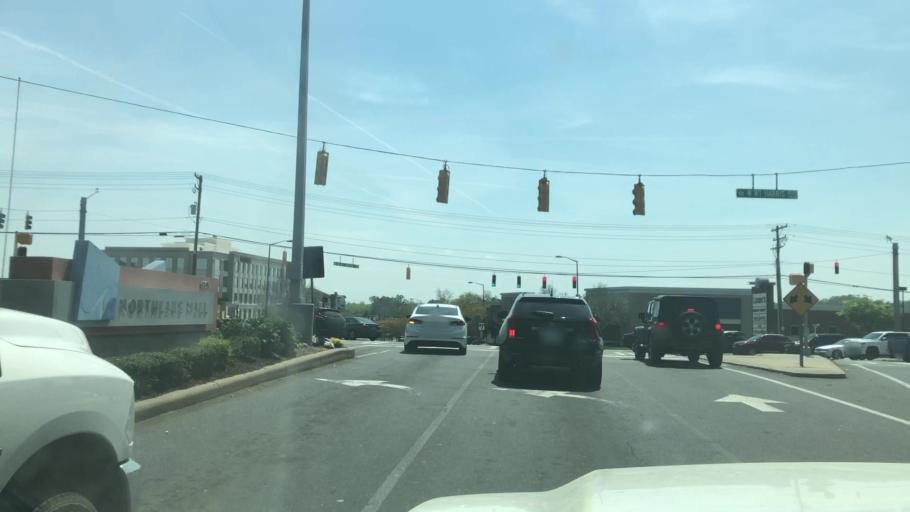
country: US
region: North Carolina
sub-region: Mecklenburg County
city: Huntersville
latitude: 35.3492
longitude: -80.8527
